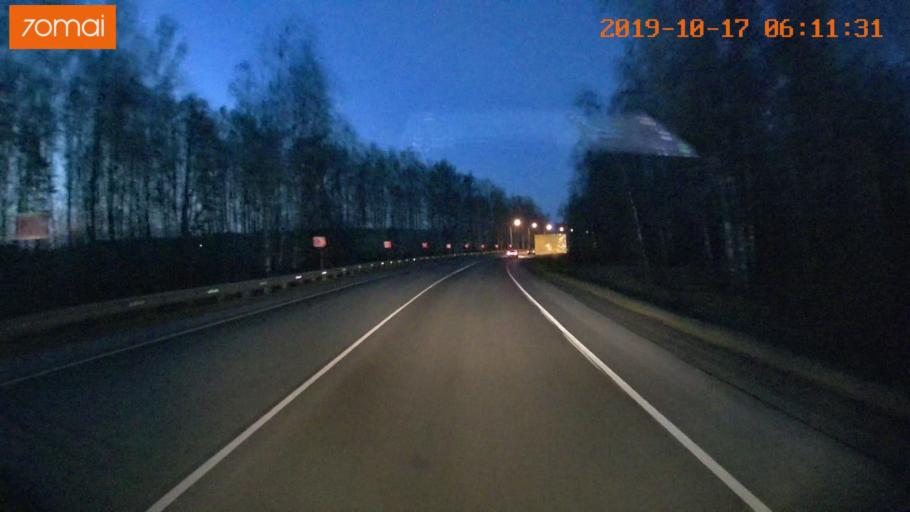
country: RU
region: Ivanovo
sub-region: Gorod Ivanovo
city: Ivanovo
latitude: 56.9181
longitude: 40.9574
